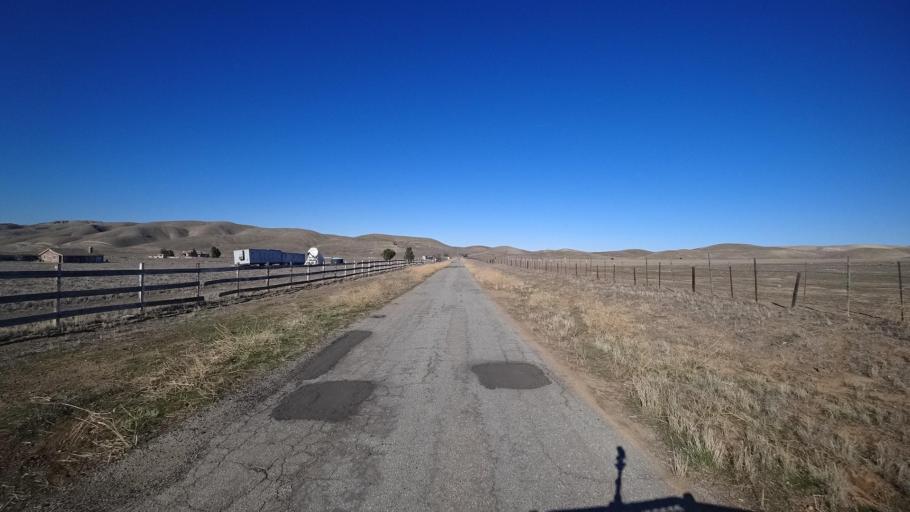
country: US
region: California
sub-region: Kern County
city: Maricopa
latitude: 34.9409
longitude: -119.4553
